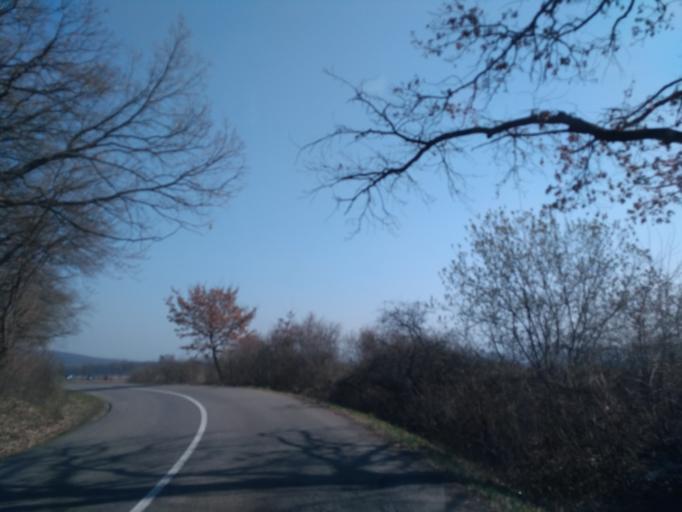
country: SK
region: Kosicky
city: Secovce
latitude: 48.7332
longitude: 21.5974
